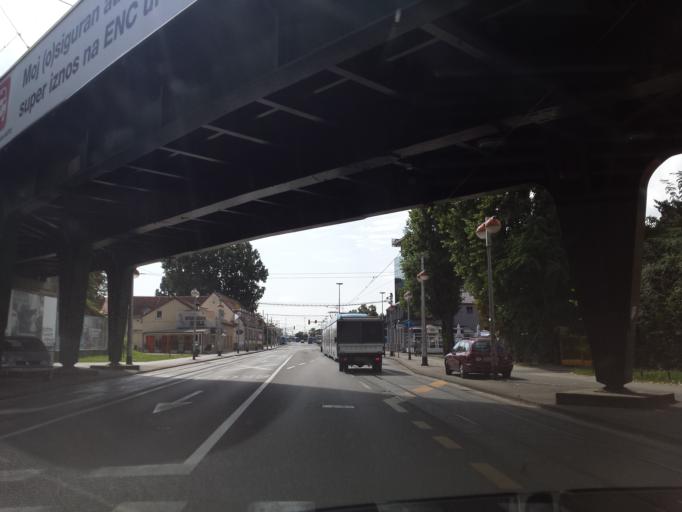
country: HR
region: Grad Zagreb
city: Novi Zagreb
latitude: 45.7883
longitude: 15.9547
